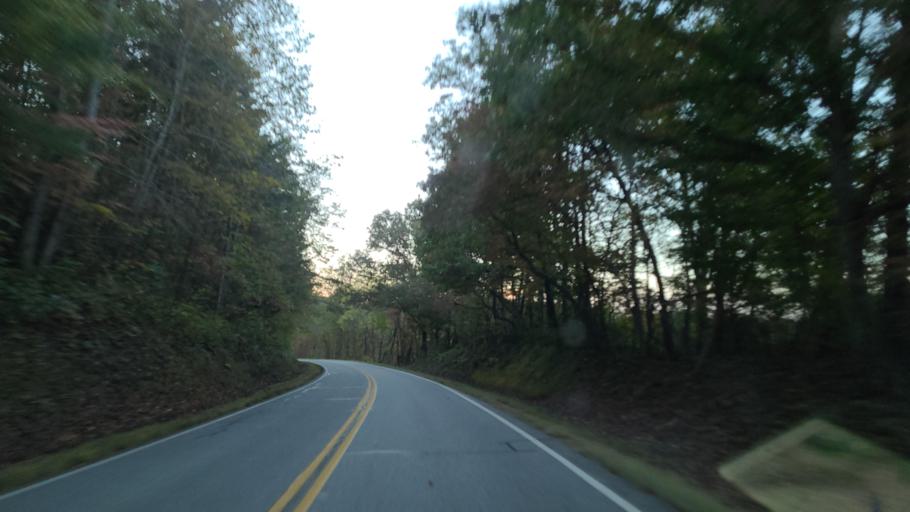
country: US
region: North Carolina
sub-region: Clay County
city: Hayesville
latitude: 34.9533
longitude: -83.8605
